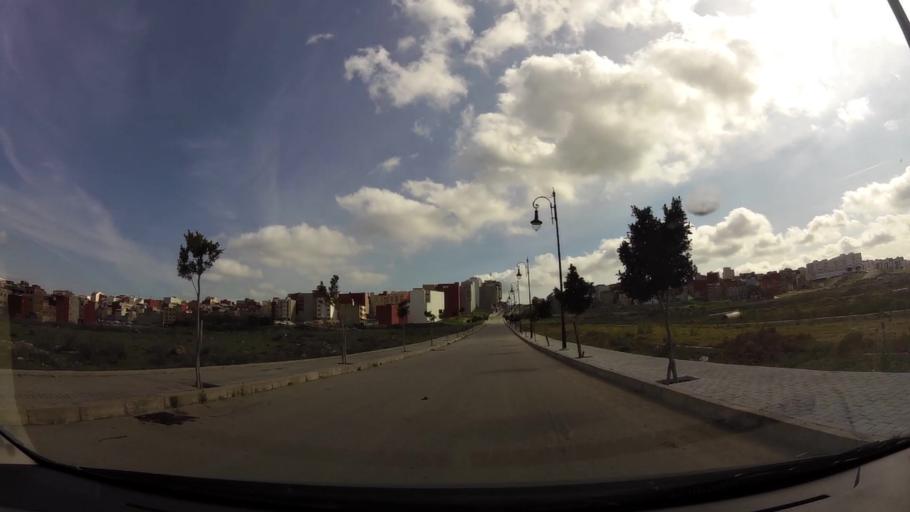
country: MA
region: Tanger-Tetouan
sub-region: Tanger-Assilah
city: Tangier
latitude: 35.7643
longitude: -5.7695
